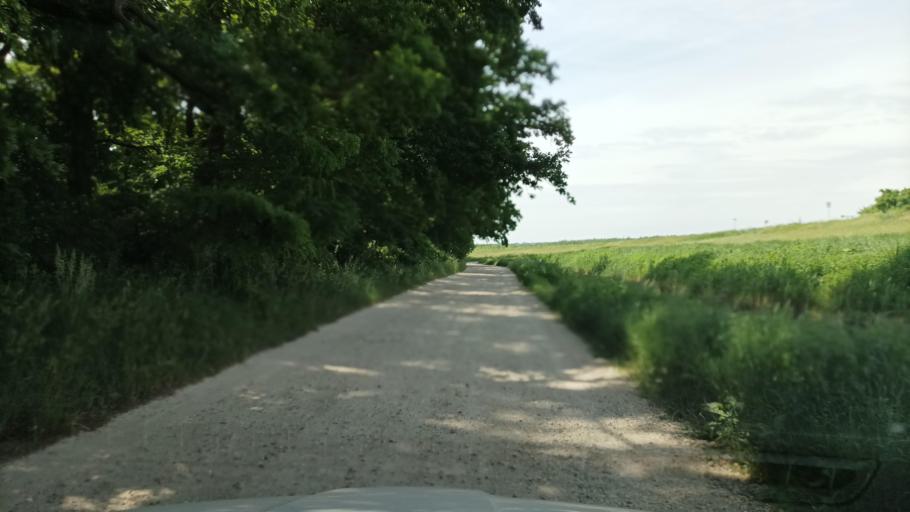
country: HU
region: Fejer
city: Racalmas
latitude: 47.0729
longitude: 18.9543
